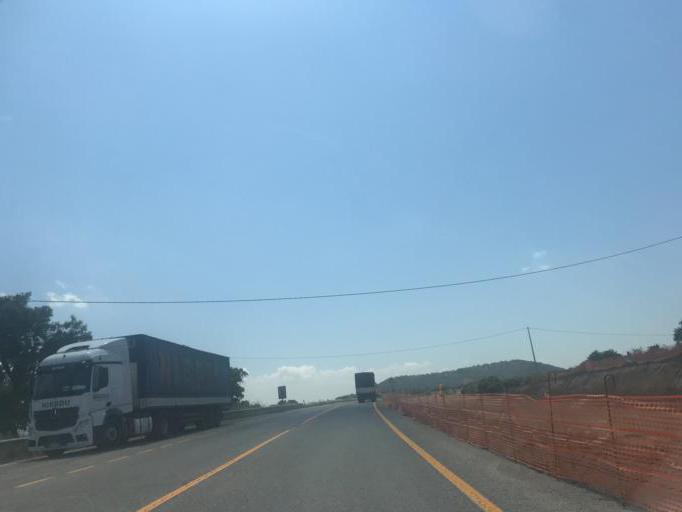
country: IT
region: Sardinia
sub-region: Provincia di Olbia-Tempio
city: Berchidda
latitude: 40.7808
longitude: 9.2451
